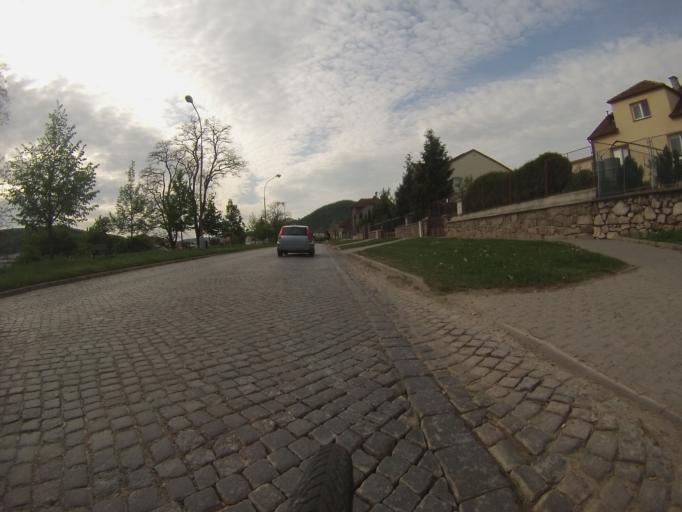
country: CZ
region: South Moravian
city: Tisnov
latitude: 49.3420
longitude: 16.4311
